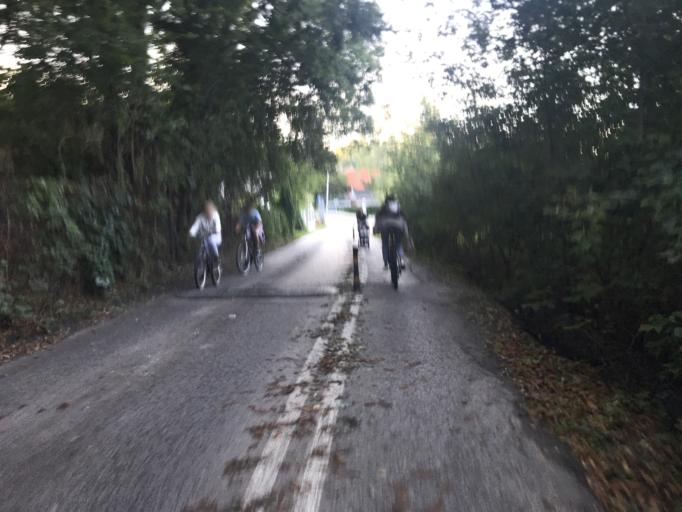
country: PL
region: Masovian Voivodeship
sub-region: Warszawa
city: Ursynow
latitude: 52.1547
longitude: 21.0608
